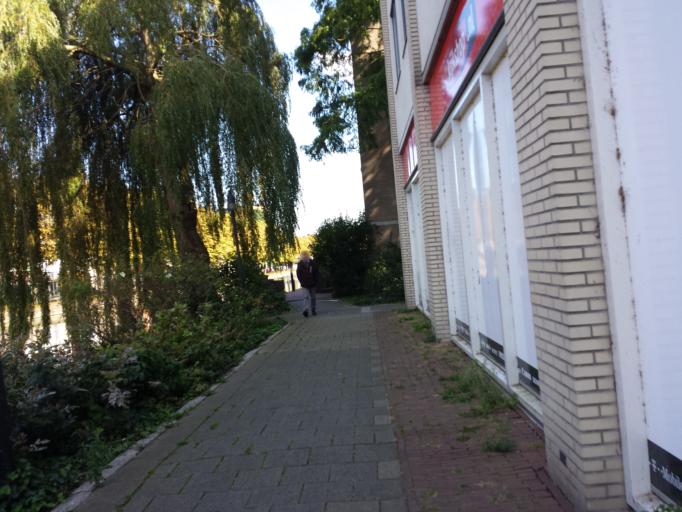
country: NL
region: South Holland
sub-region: Gemeente Gouda
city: Gouda
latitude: 52.0149
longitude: 4.7113
